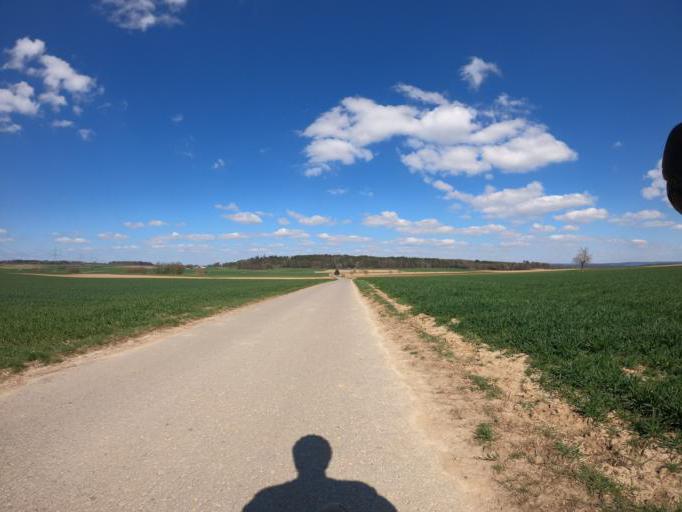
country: DE
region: Baden-Wuerttemberg
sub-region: Regierungsbezirk Stuttgart
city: Bondorf
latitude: 48.4750
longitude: 8.8657
